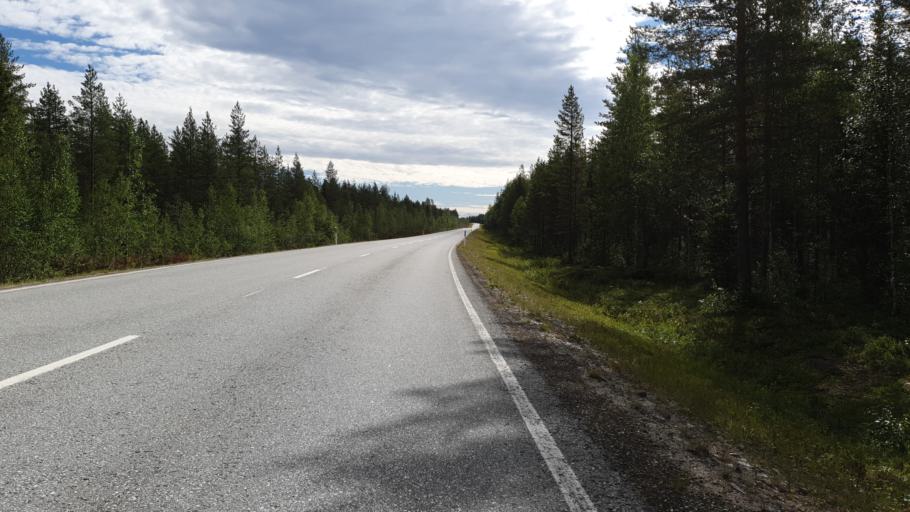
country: FI
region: Kainuu
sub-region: Kehys-Kainuu
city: Kuhmo
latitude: 64.4913
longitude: 29.8366
